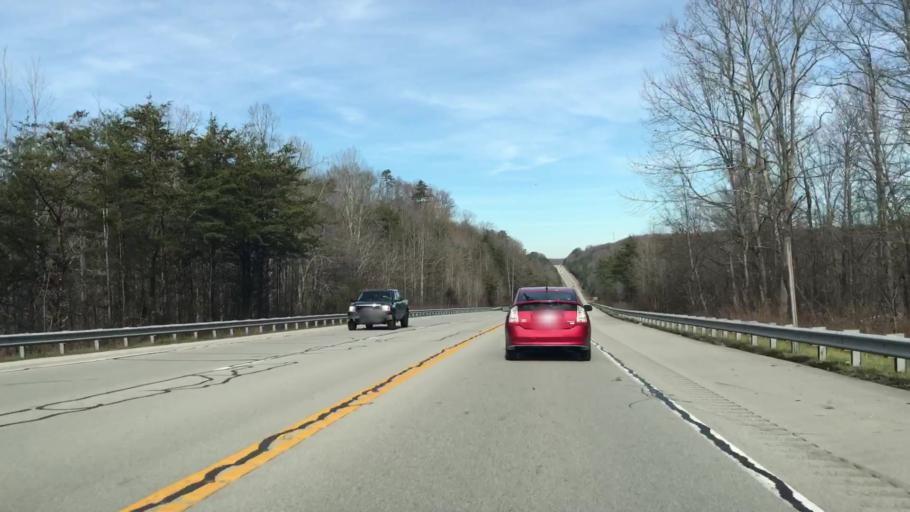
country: US
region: Kentucky
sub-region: McCreary County
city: Whitley City
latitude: 36.8137
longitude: -84.4878
